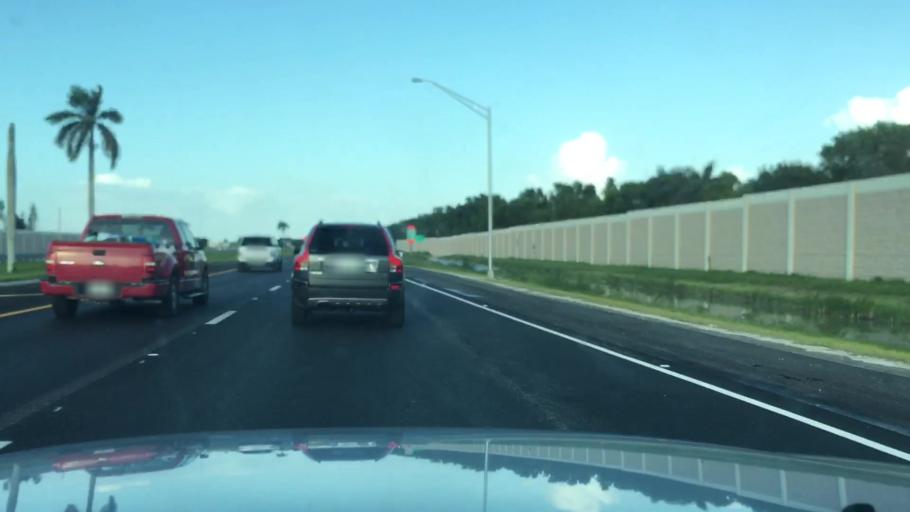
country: US
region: Florida
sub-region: Miami-Dade County
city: Leisure City
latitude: 25.4821
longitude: -80.4309
